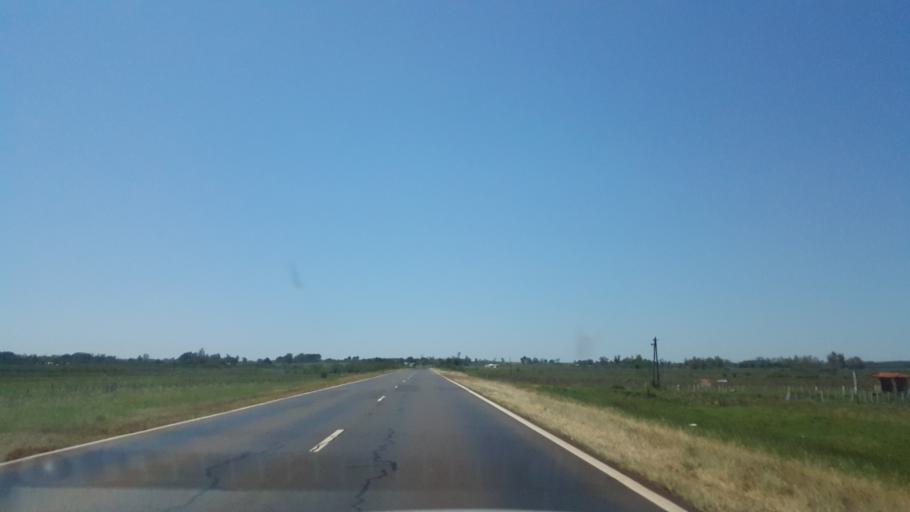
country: AR
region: Corrientes
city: Santo Tome
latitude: -28.5334
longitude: -56.1022
